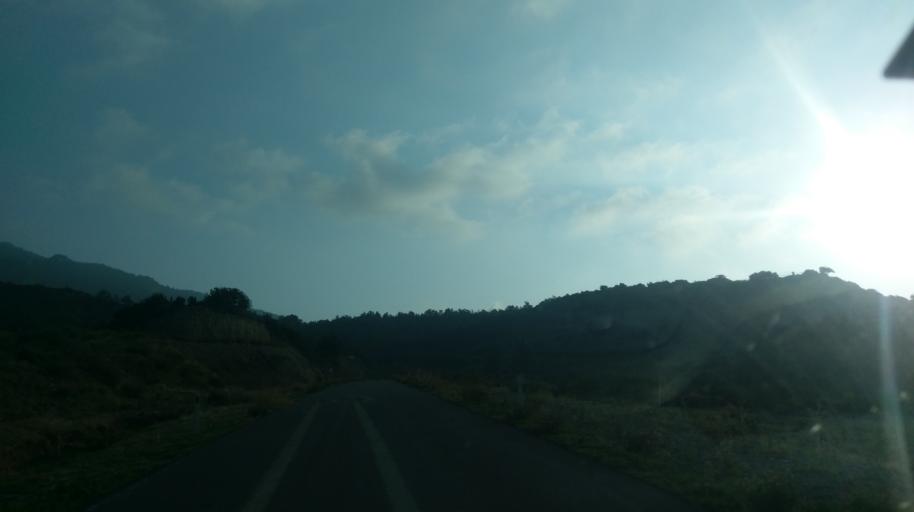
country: CY
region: Ammochostos
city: Trikomo
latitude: 35.4193
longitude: 33.9076
